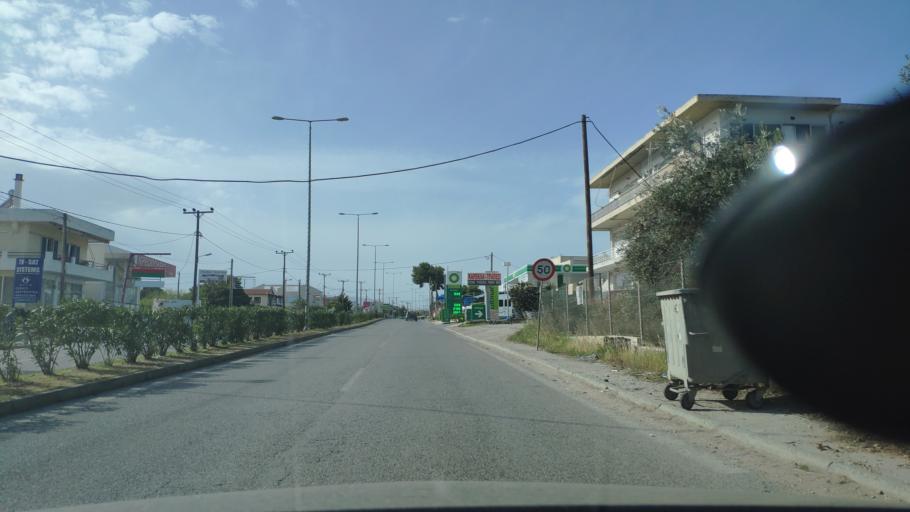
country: GR
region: Attica
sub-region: Nomarchia Anatolikis Attikis
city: Limin Mesoyaias
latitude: 37.8911
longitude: 23.9955
